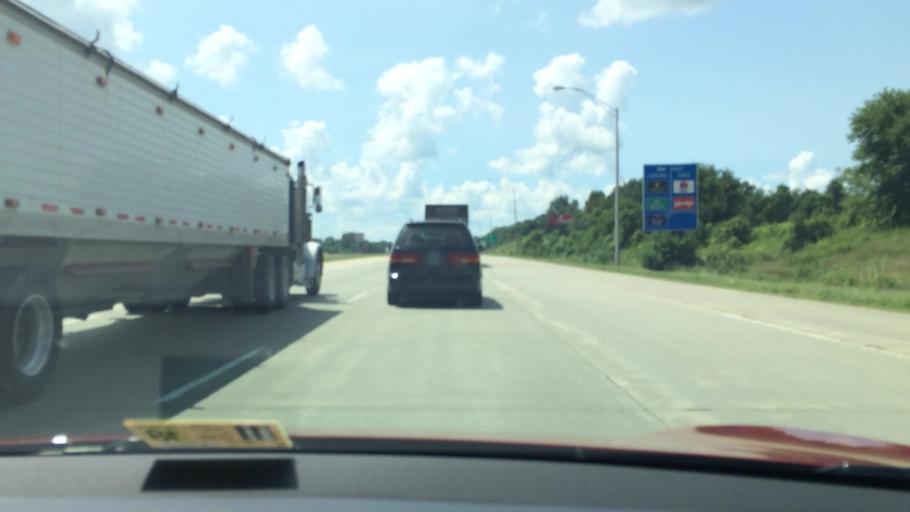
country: US
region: Indiana
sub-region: Saint Joseph County
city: South Bend
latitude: 41.7219
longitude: -86.3395
